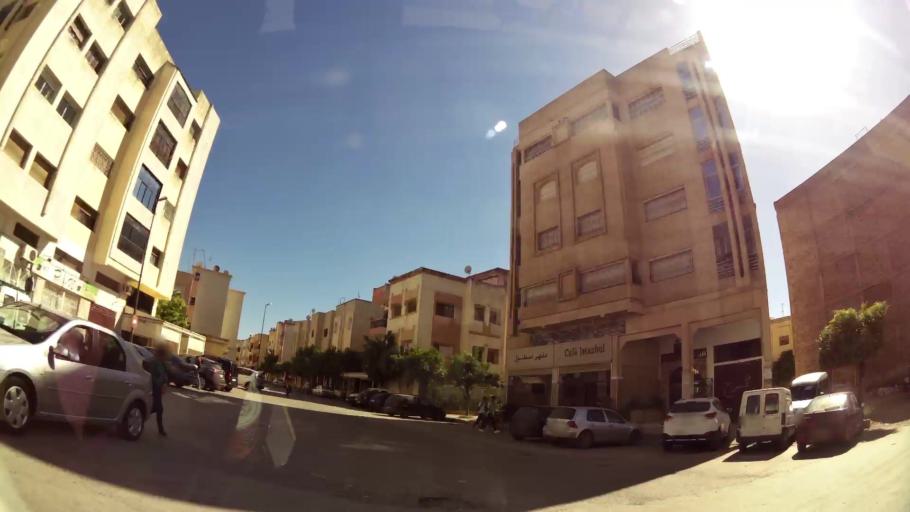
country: MA
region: Fes-Boulemane
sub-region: Fes
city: Fes
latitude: 34.0173
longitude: -4.9796
